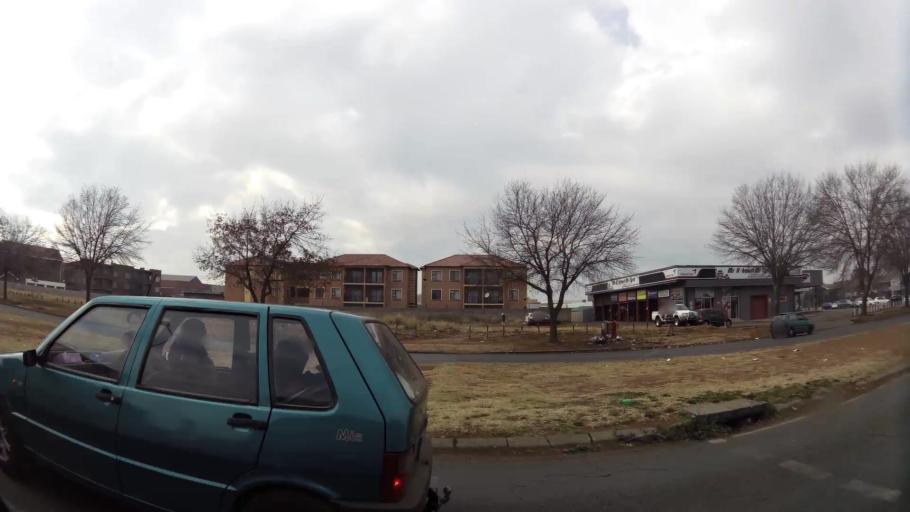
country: ZA
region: Gauteng
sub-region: Sedibeng District Municipality
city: Vanderbijlpark
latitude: -26.6968
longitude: 27.8323
